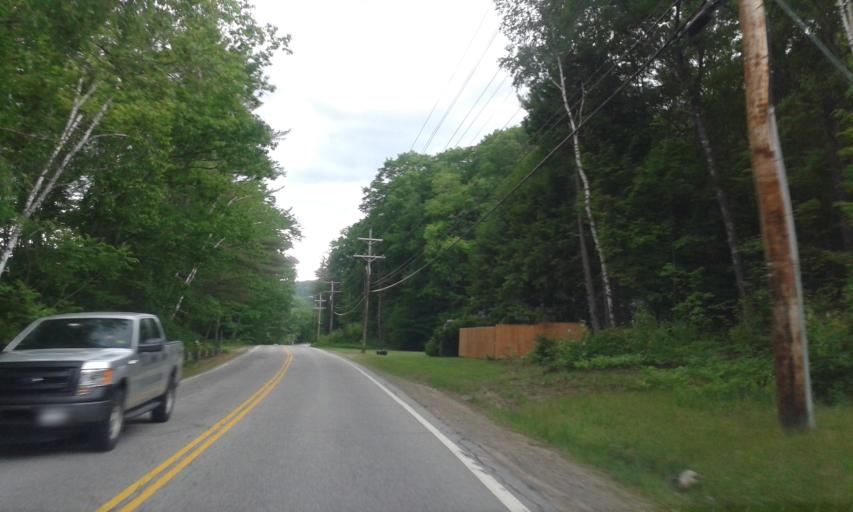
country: US
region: New Hampshire
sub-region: Grafton County
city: Woodstock
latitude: 44.0160
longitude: -71.6845
